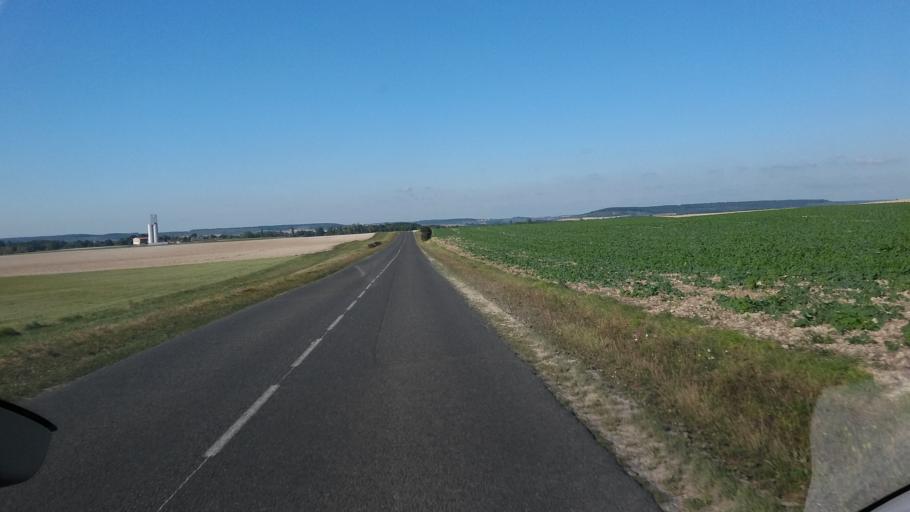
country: FR
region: Champagne-Ardenne
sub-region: Departement de la Marne
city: Connantre
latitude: 48.7731
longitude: 3.8667
